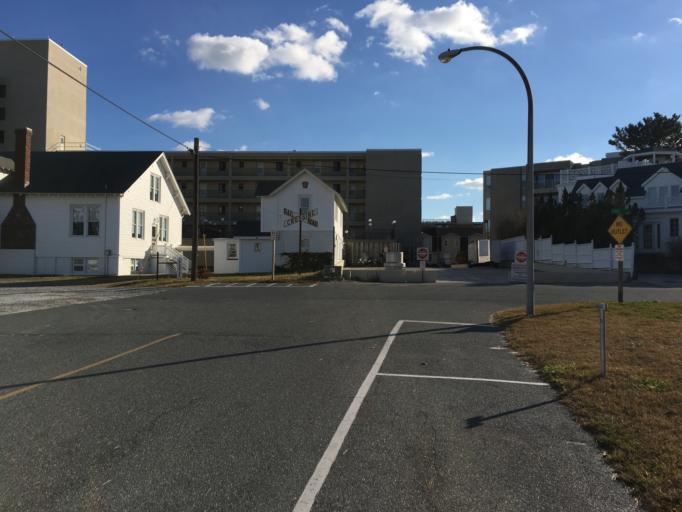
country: US
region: Delaware
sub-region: Sussex County
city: Rehoboth Beach
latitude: 38.7208
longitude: -75.0779
